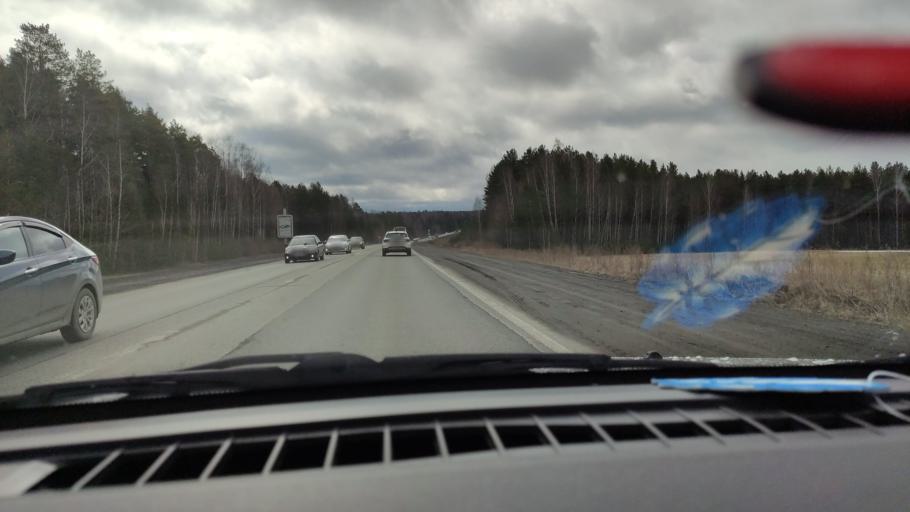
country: RU
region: Sverdlovsk
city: Talitsa
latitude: 56.8662
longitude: 60.0465
